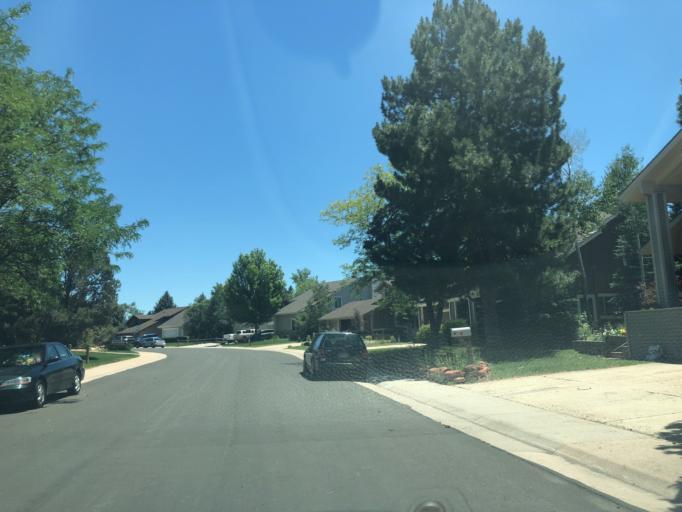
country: US
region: Colorado
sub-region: Arapahoe County
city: Dove Valley
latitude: 39.6164
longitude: -104.7791
